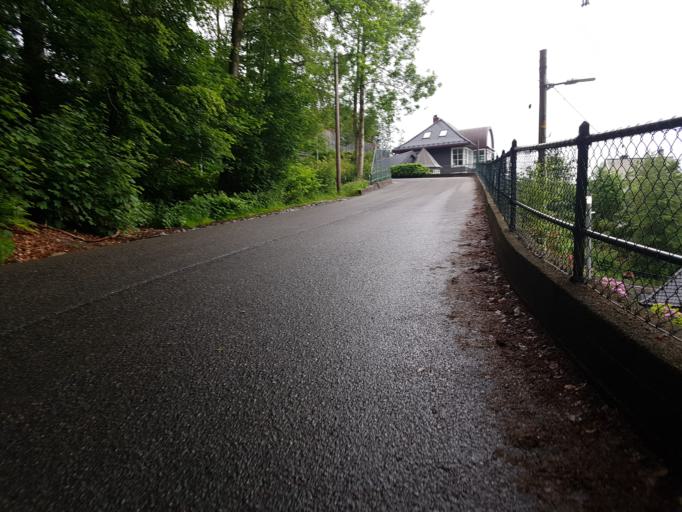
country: NO
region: Hordaland
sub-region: Bergen
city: Bergen
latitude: 60.3959
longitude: 5.3347
